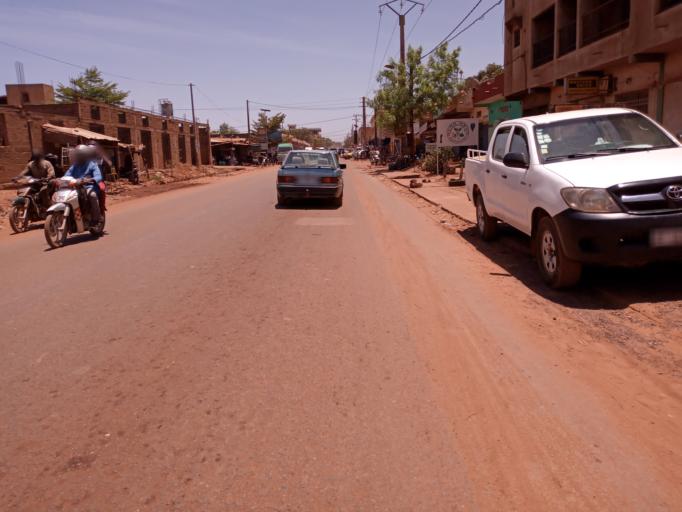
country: ML
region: Bamako
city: Bamako
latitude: 12.5883
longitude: -7.9738
